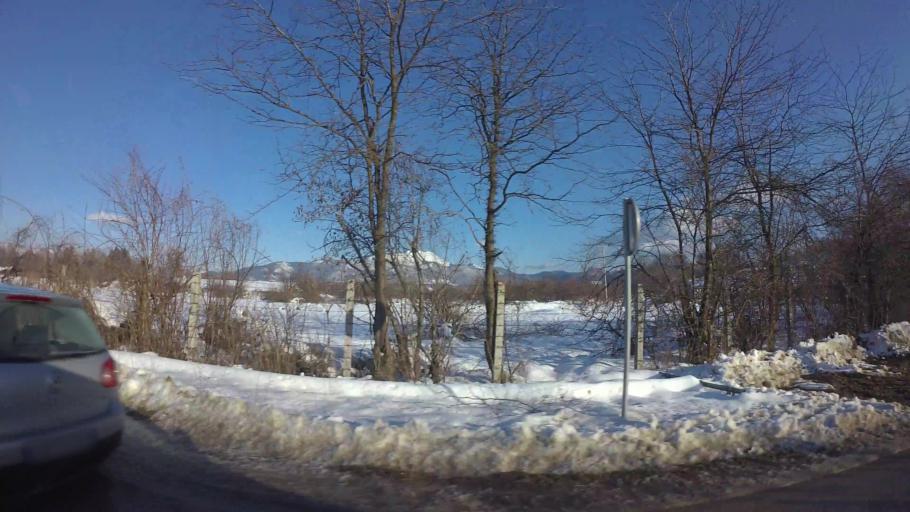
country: BA
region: Federation of Bosnia and Herzegovina
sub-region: Kanton Sarajevo
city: Sarajevo
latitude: 43.8129
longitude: 18.3462
